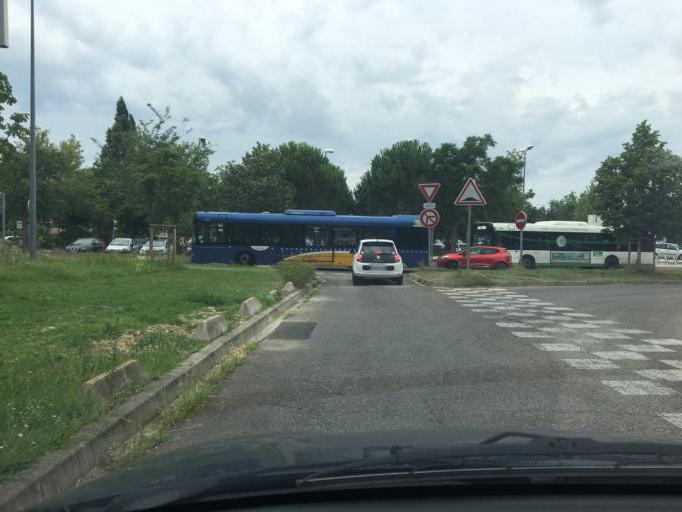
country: FR
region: Provence-Alpes-Cote d'Azur
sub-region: Departement des Bouches-du-Rhone
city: Rognonas
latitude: 43.9186
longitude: 4.8045
